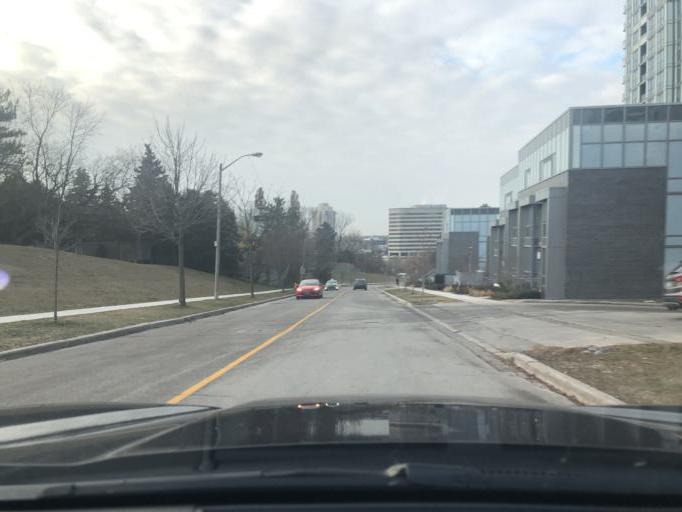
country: CA
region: Ontario
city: Willowdale
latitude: 43.7632
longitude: -79.3451
